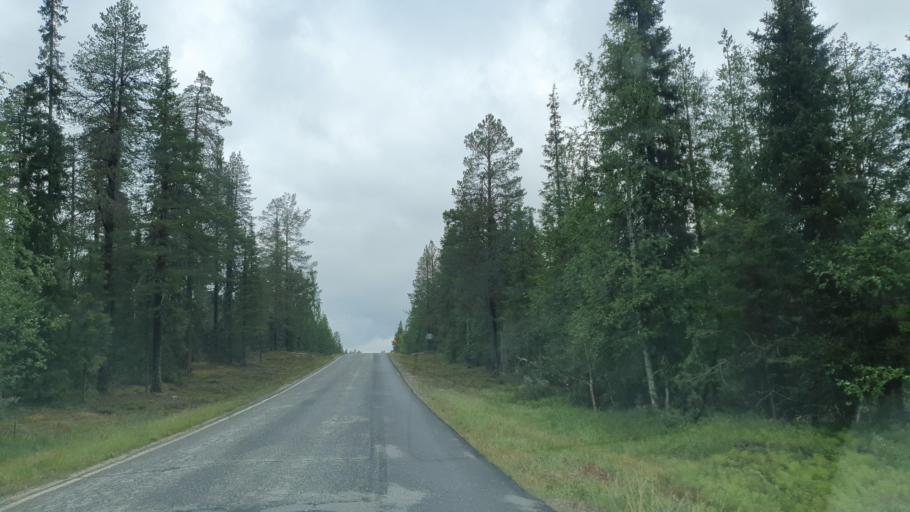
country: FI
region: Lapland
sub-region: Tunturi-Lappi
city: Kolari
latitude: 67.6747
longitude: 24.1451
